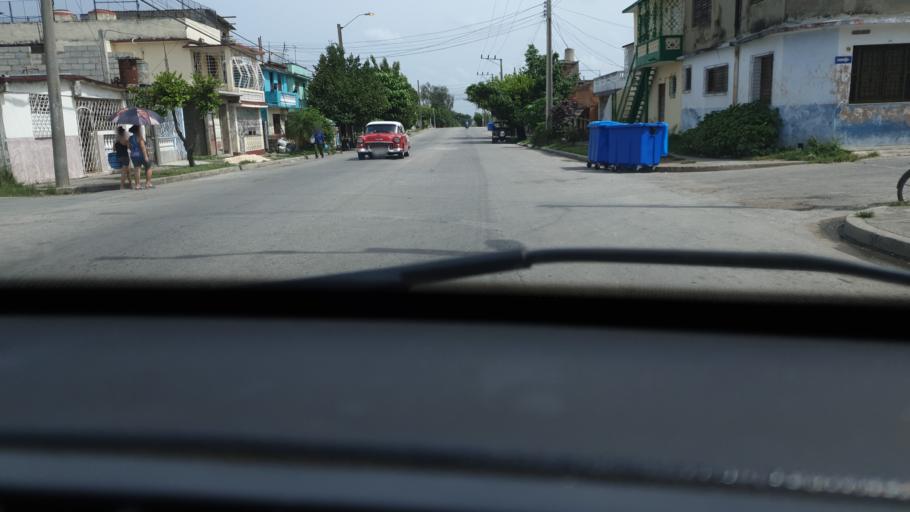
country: CU
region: Villa Clara
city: Santa Clara
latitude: 22.3891
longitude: -79.9597
